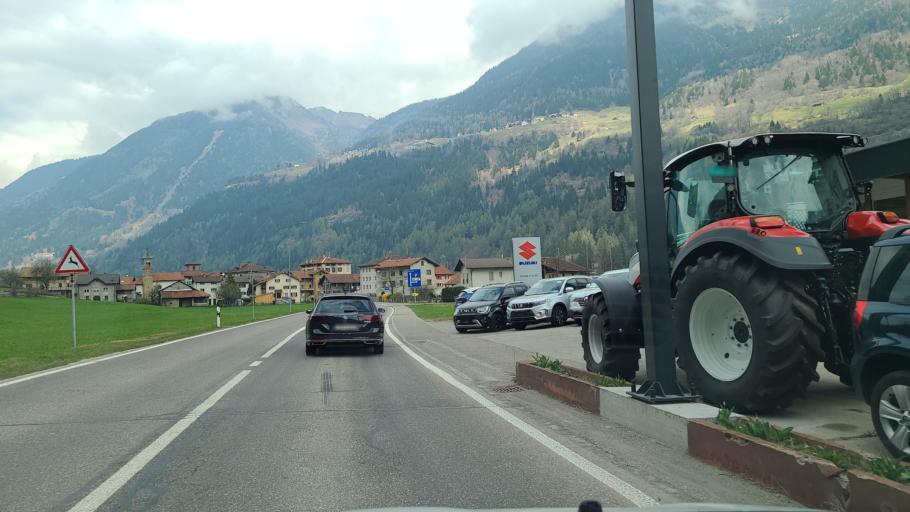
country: CH
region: Ticino
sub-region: Leventina District
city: Airolo
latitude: 46.5064
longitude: 8.7054
